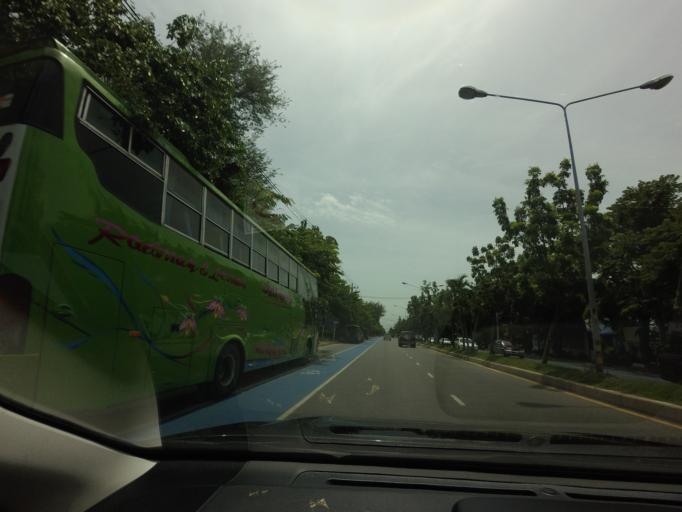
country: TH
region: Chon Buri
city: Chon Buri
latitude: 13.2977
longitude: 100.9073
